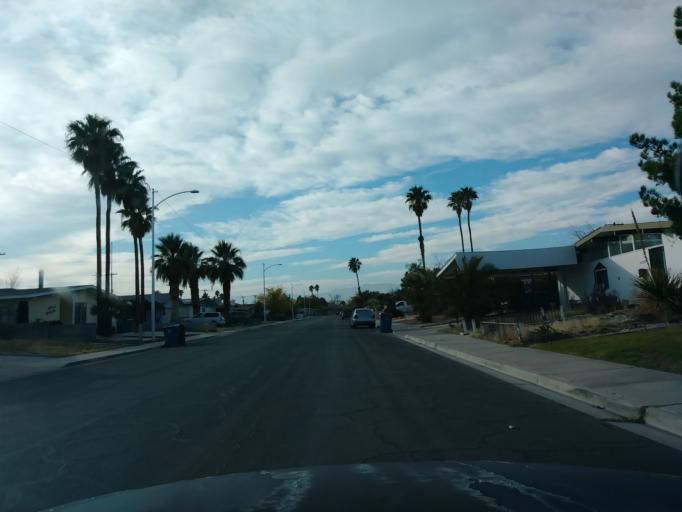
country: US
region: Nevada
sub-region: Clark County
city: Spring Valley
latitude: 36.1686
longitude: -115.2293
